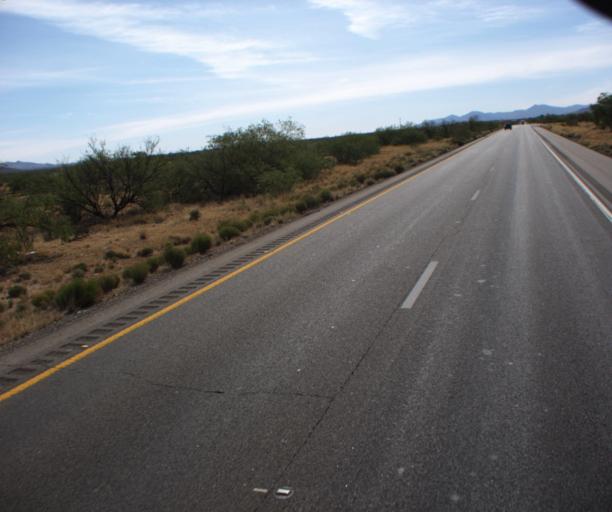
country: US
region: Arizona
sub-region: Pima County
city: Vail
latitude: 32.0266
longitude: -110.7201
